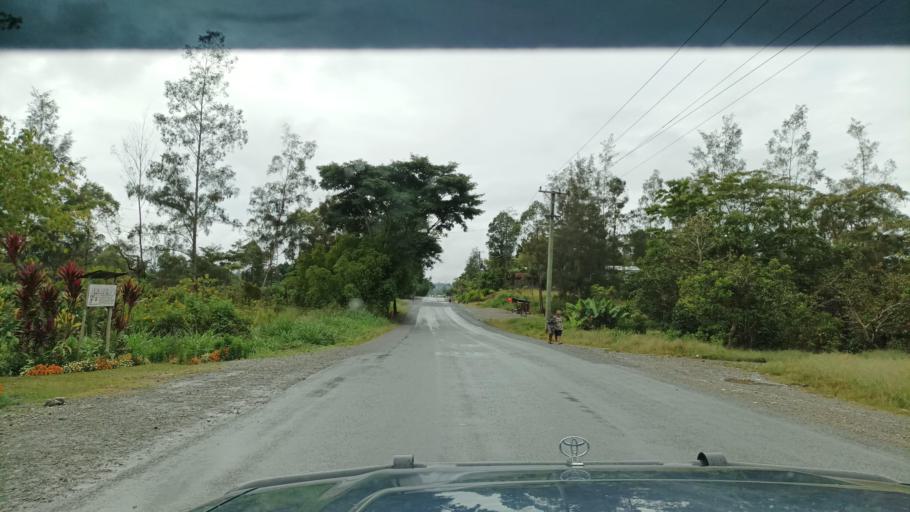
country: PG
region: Jiwaka
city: Minj
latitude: -5.8560
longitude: 144.6320
